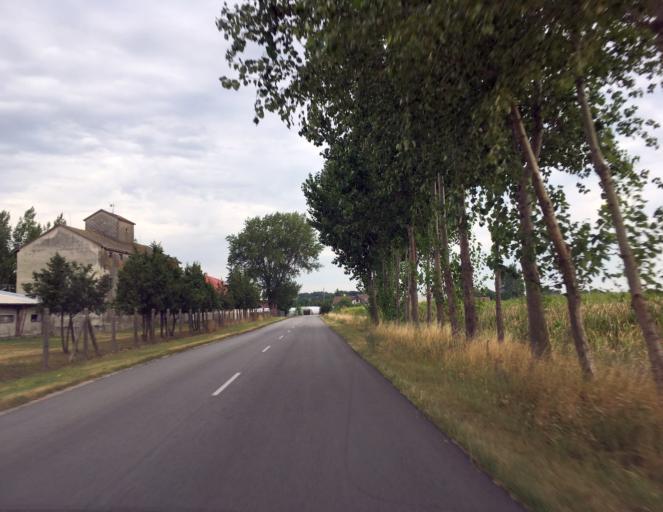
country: SK
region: Trnavsky
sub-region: Okres Dunajska Streda
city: Velky Meder
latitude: 47.9242
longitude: 17.6988
